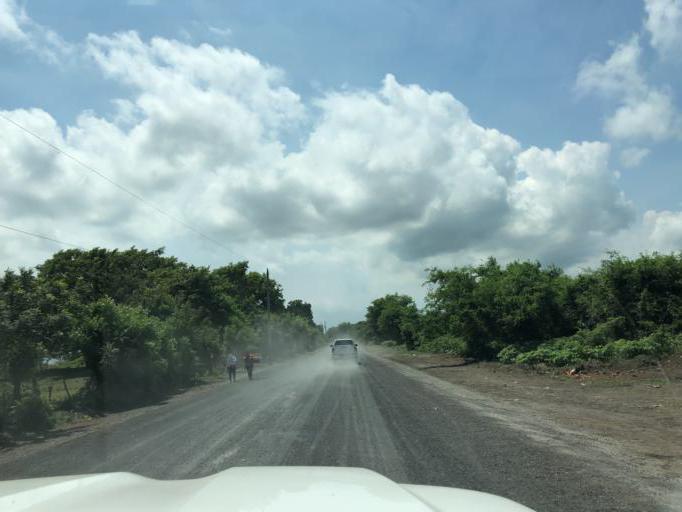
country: NI
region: Masaya
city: Tisma
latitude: 12.0512
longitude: -85.9160
